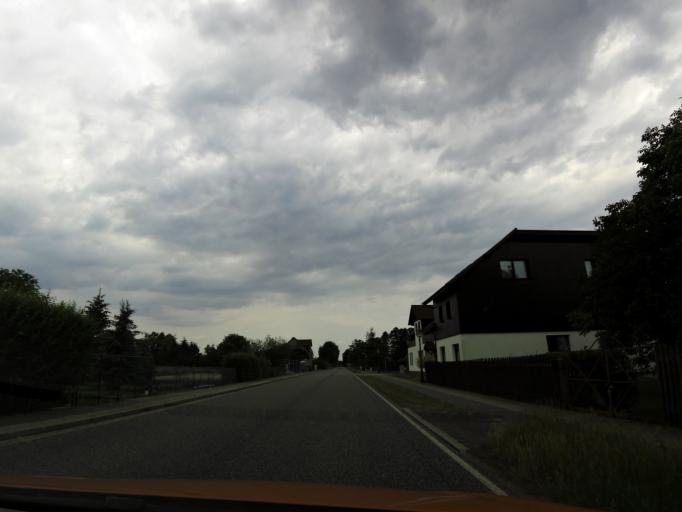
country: DE
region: Brandenburg
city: Baruth
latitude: 52.0539
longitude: 13.5059
